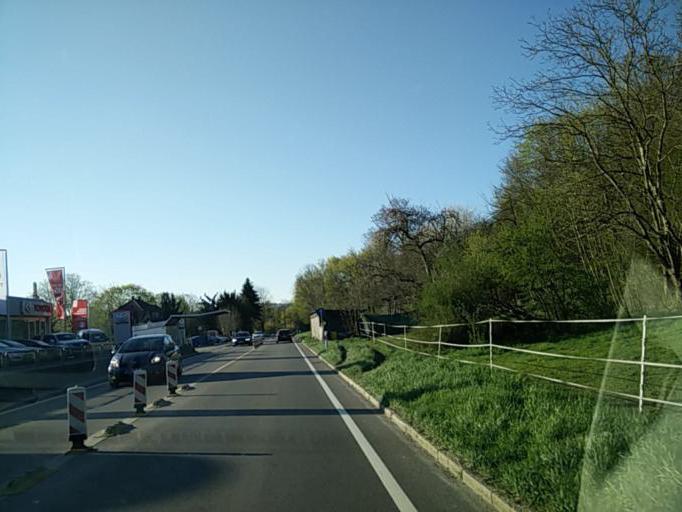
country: DE
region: Baden-Wuerttemberg
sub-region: Tuebingen Region
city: Tuebingen
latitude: 48.5023
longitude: 9.0604
